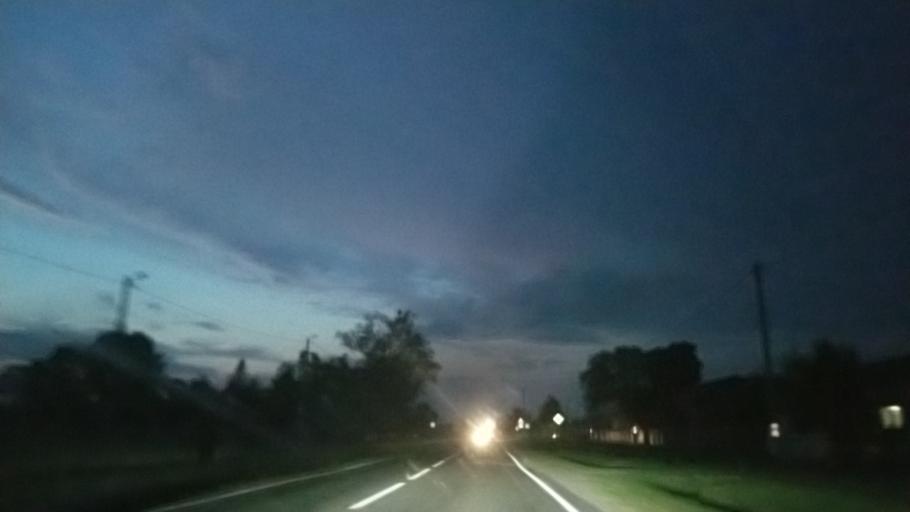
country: PL
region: Lublin Voivodeship
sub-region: Powiat bialski
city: Koden
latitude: 51.9287
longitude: 23.6602
